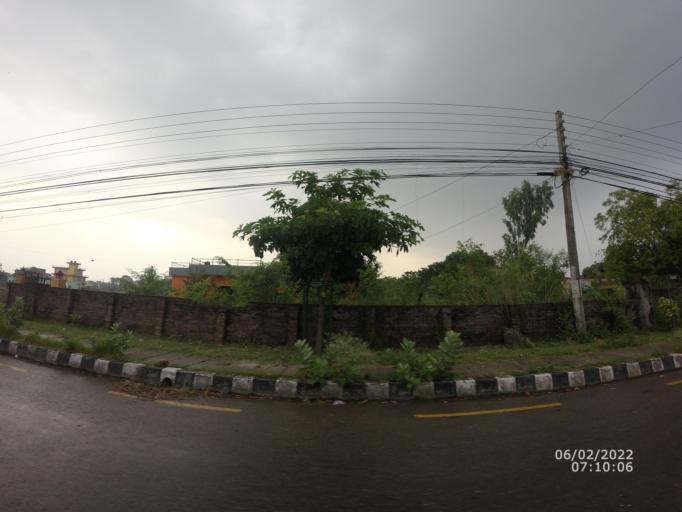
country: NP
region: Western Region
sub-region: Lumbini Zone
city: Bhairahawa
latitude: 27.4920
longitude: 83.4451
